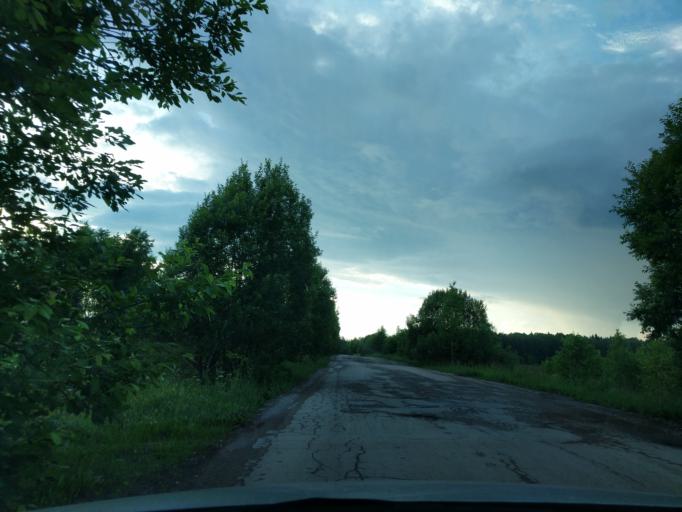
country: RU
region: Kaluga
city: Myatlevo
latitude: 54.8557
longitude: 35.5806
